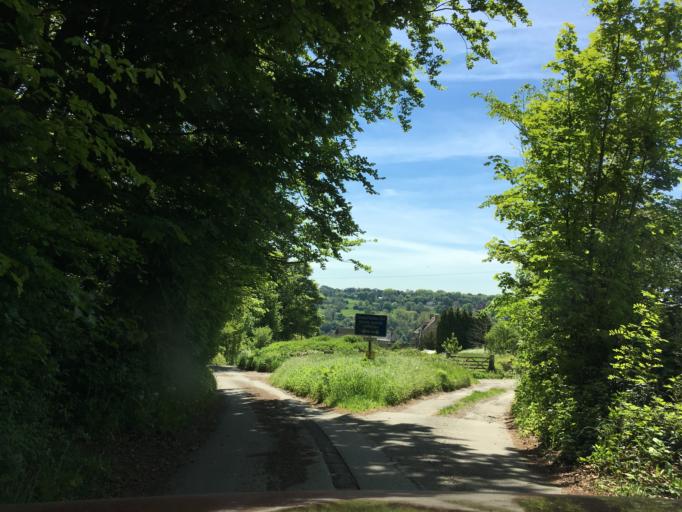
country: GB
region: England
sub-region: Gloucestershire
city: Brimscombe
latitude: 51.7246
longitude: -2.1859
